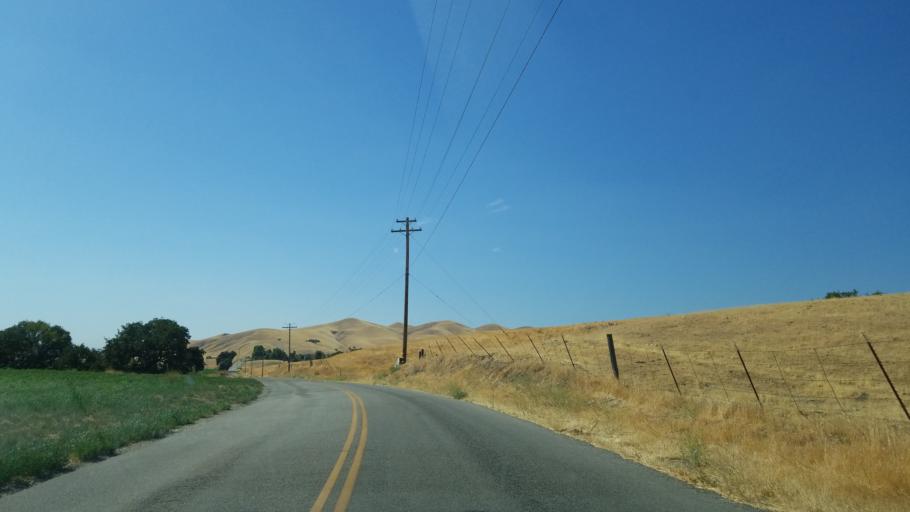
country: US
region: California
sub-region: San Luis Obispo County
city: San Miguel
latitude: 35.7681
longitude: -120.6879
